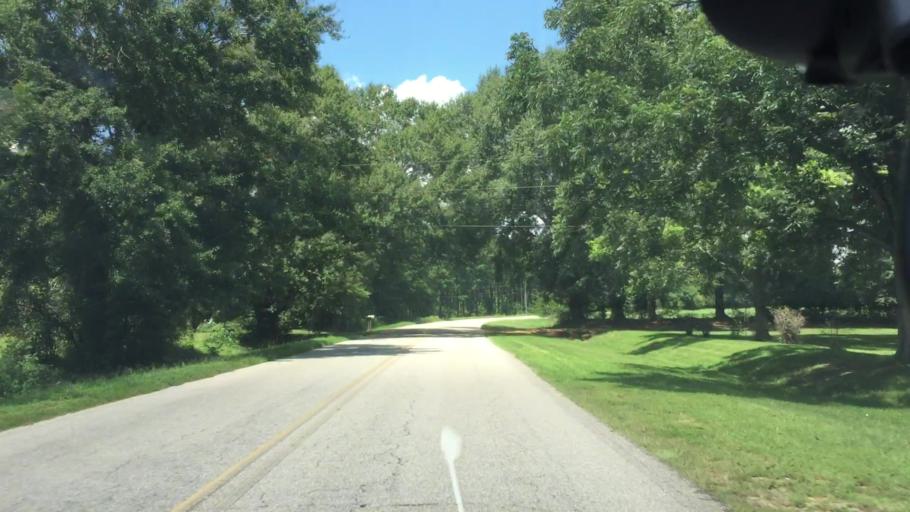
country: US
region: Alabama
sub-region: Pike County
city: Troy
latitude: 31.7530
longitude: -85.9847
